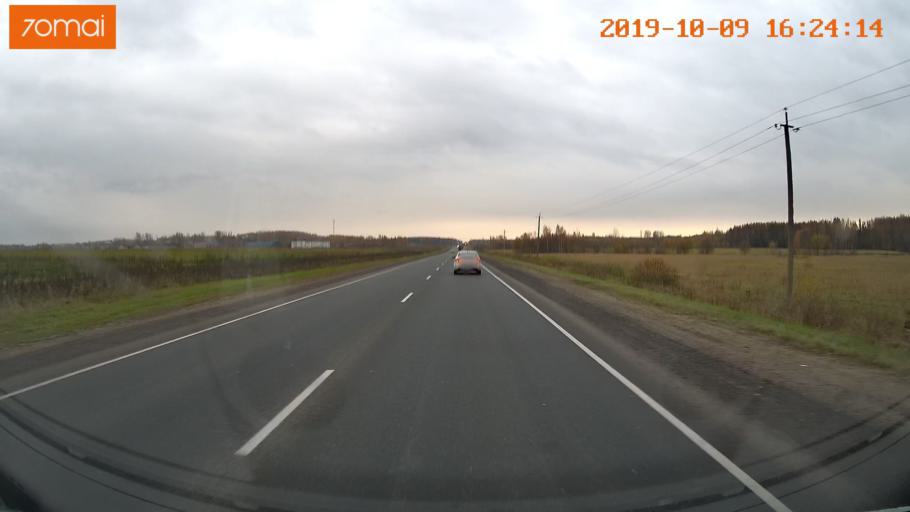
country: RU
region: Kostroma
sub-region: Kostromskoy Rayon
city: Kostroma
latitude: 57.6547
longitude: 40.9086
